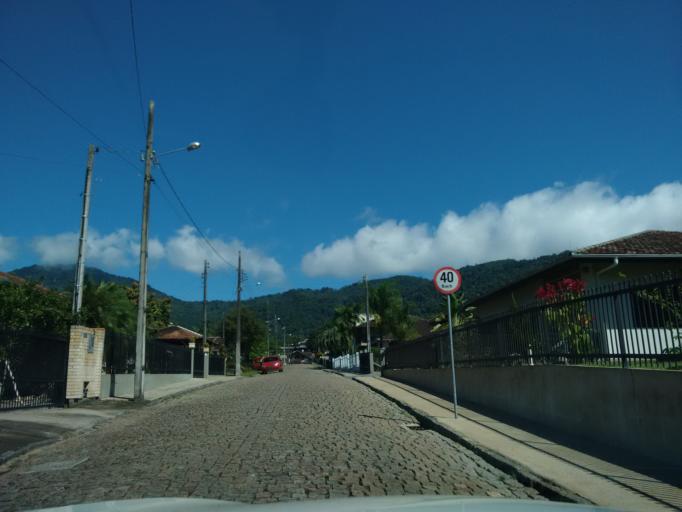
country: BR
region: Santa Catarina
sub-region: Pomerode
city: Pomerode
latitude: -26.7487
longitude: -49.1717
